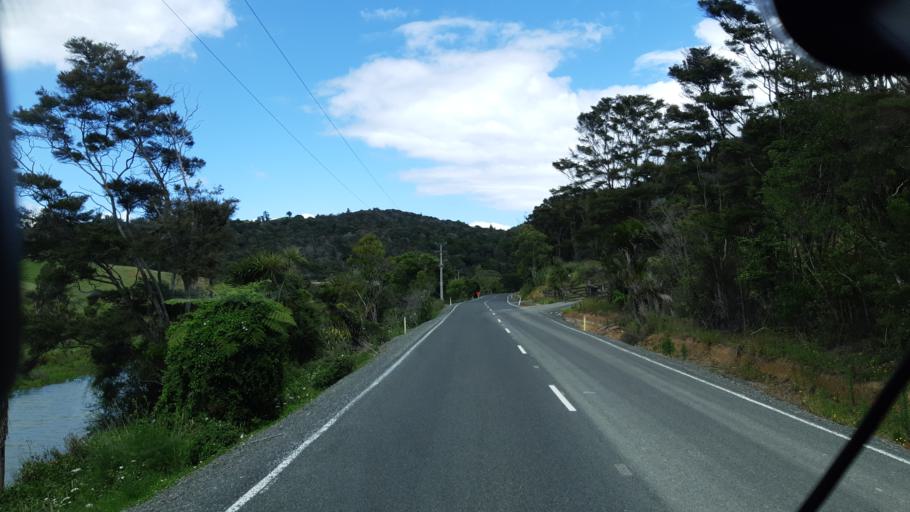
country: NZ
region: Northland
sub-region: Far North District
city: Taipa
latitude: -35.2418
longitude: 173.5385
